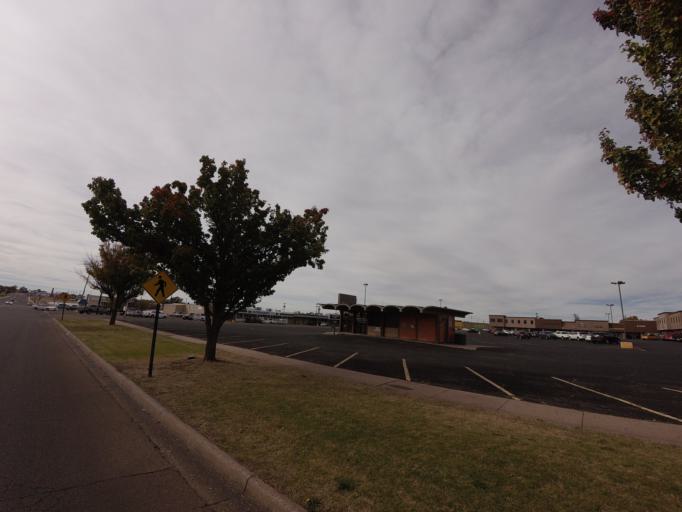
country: US
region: New Mexico
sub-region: Curry County
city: Clovis
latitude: 34.4212
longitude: -103.2054
